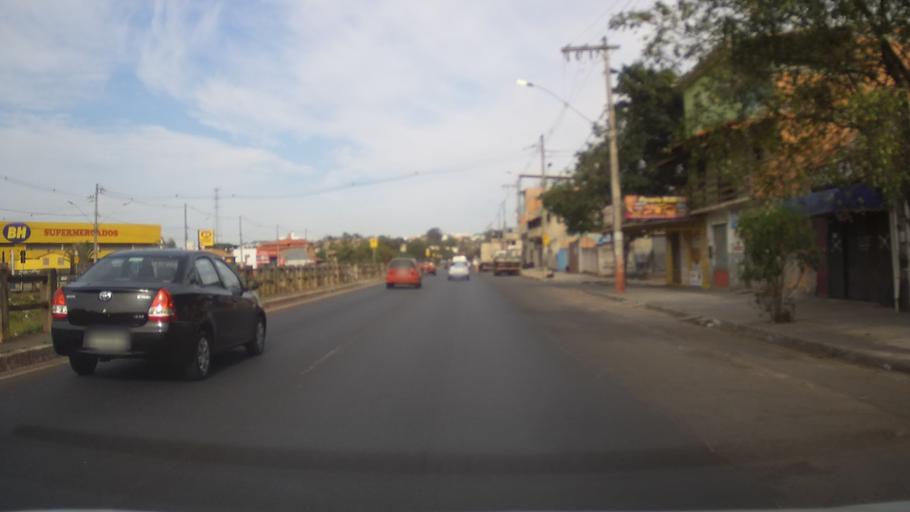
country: BR
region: Minas Gerais
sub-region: Contagem
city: Contagem
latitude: -19.8735
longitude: -44.0175
